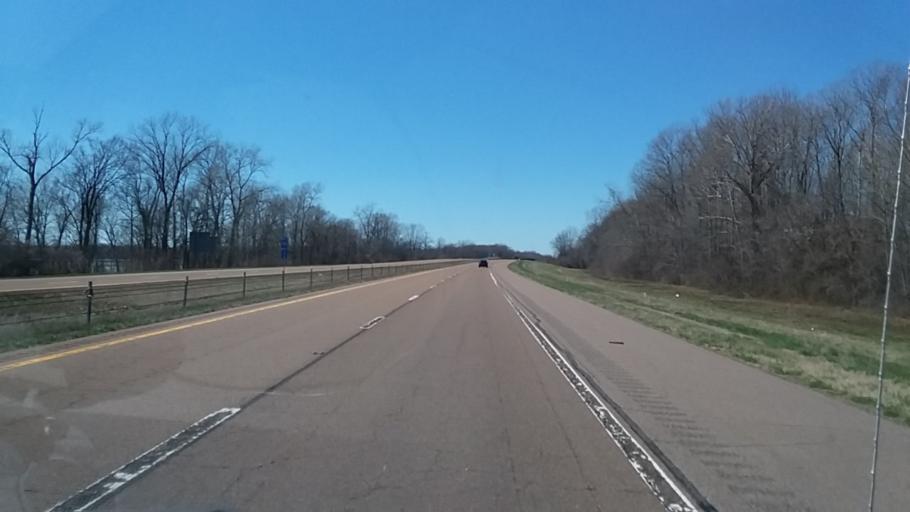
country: US
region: Tennessee
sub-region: Dyer County
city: Dyersburg
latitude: 36.0775
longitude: -89.5122
